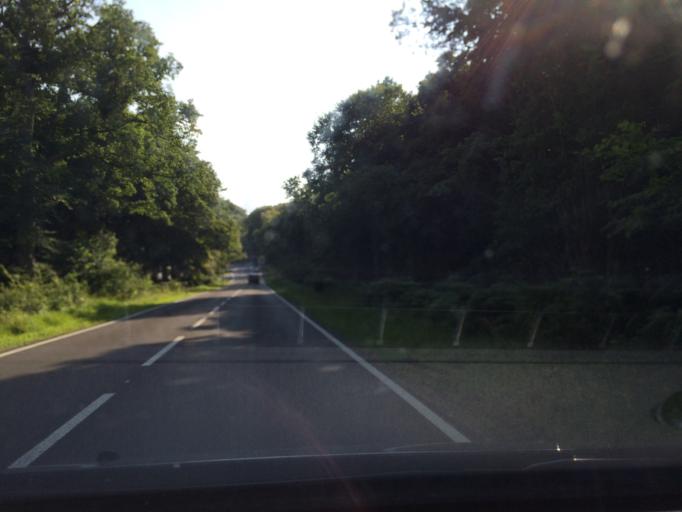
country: DE
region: Mecklenburg-Vorpommern
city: Ostseebad Binz
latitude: 54.4366
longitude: 13.5603
